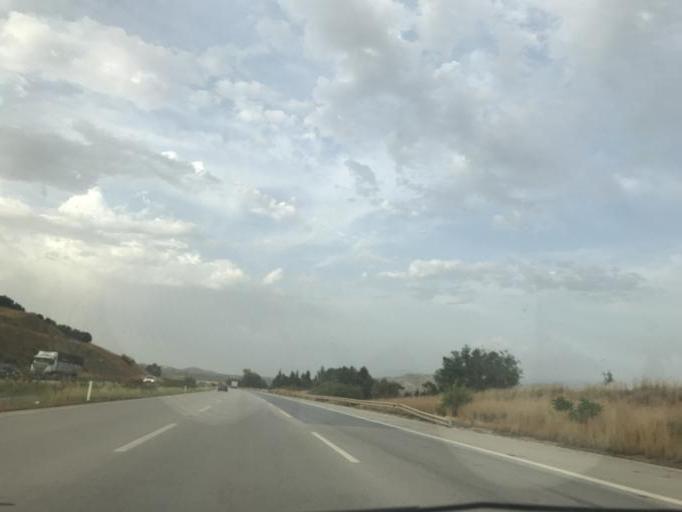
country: TR
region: Adana
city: Kosreli
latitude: 37.0159
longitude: 36.0021
